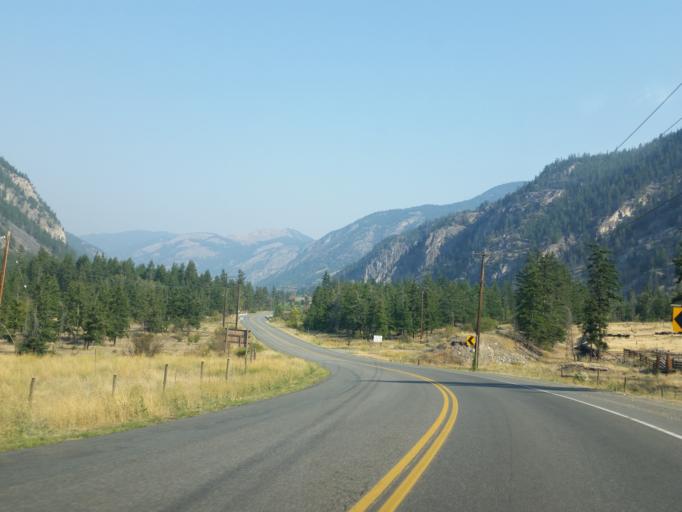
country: CA
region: British Columbia
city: Summerland
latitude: 49.3060
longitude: -120.0276
